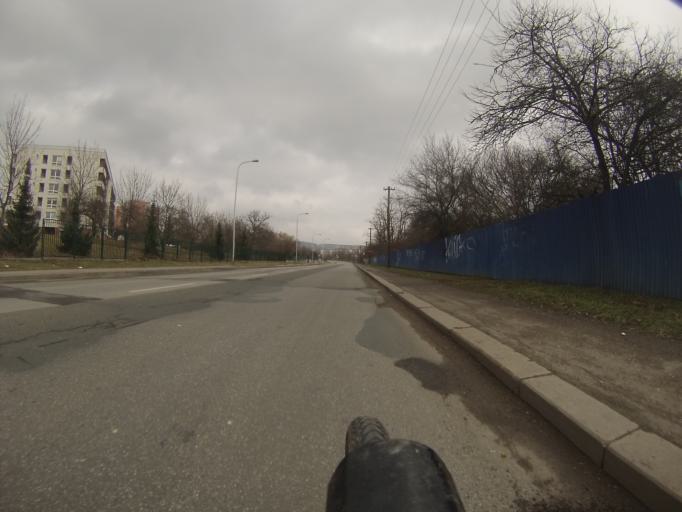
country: CZ
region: South Moravian
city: Bilovice nad Svitavou
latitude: 49.1983
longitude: 16.6620
